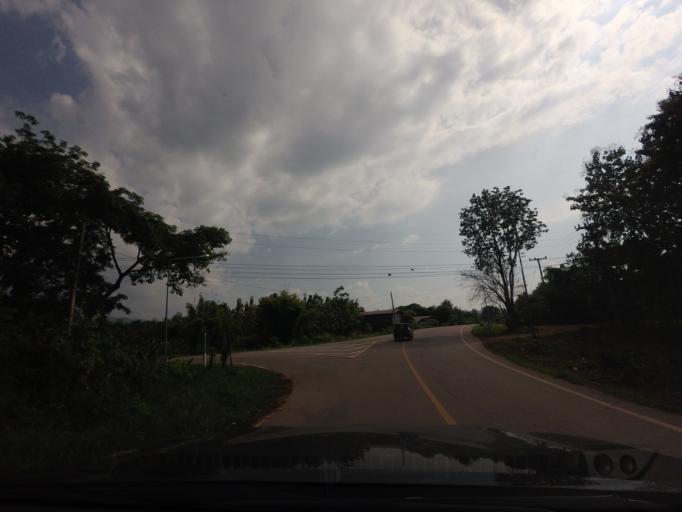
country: TH
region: Phitsanulok
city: Nakhon Thai
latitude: 17.0414
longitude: 100.9141
